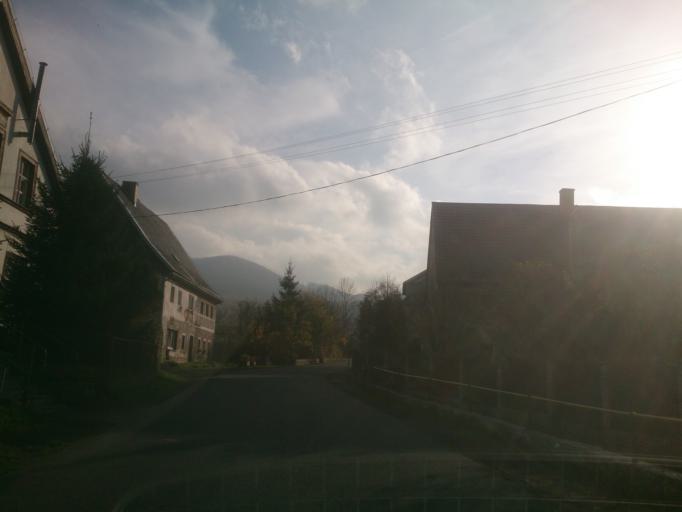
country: PL
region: Lower Silesian Voivodeship
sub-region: Powiat jeleniogorski
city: Sosnowka
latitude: 50.8212
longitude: 15.7214
